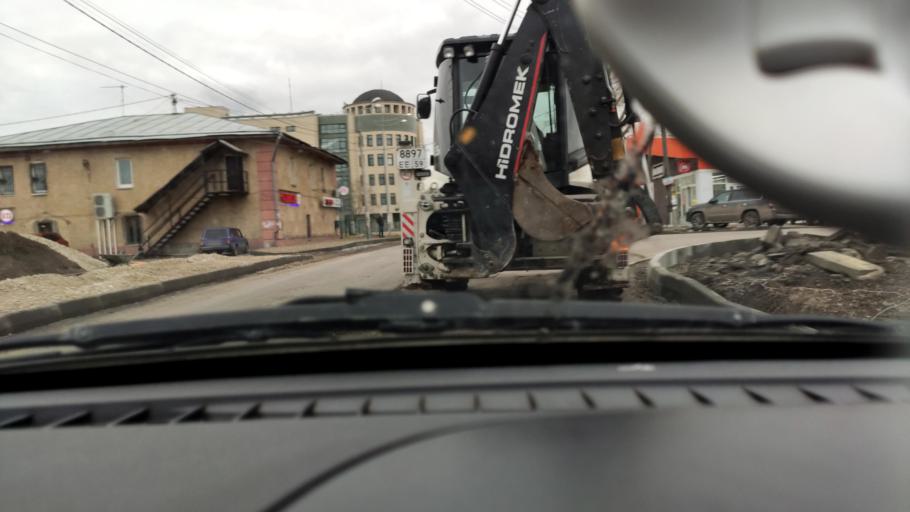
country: RU
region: Perm
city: Kondratovo
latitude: 57.9590
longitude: 56.1285
